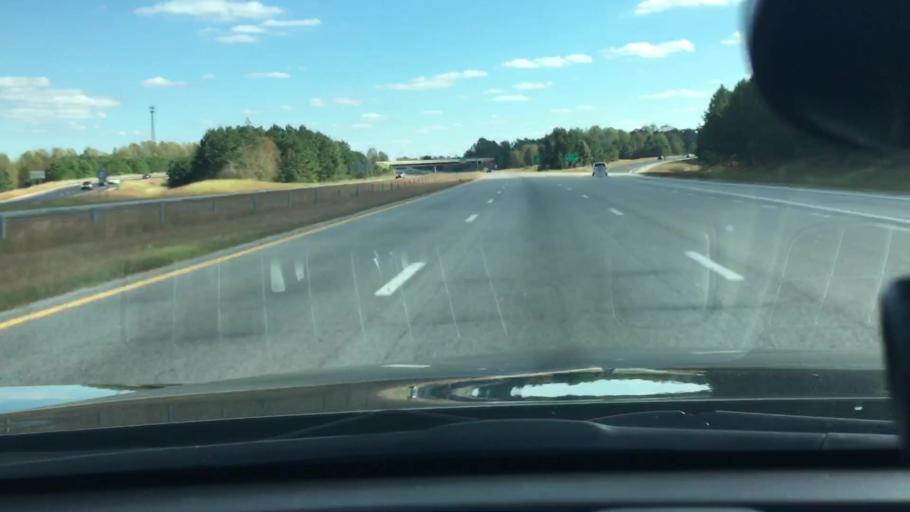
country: US
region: North Carolina
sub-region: Wilson County
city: Lucama
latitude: 35.6868
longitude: -77.9662
